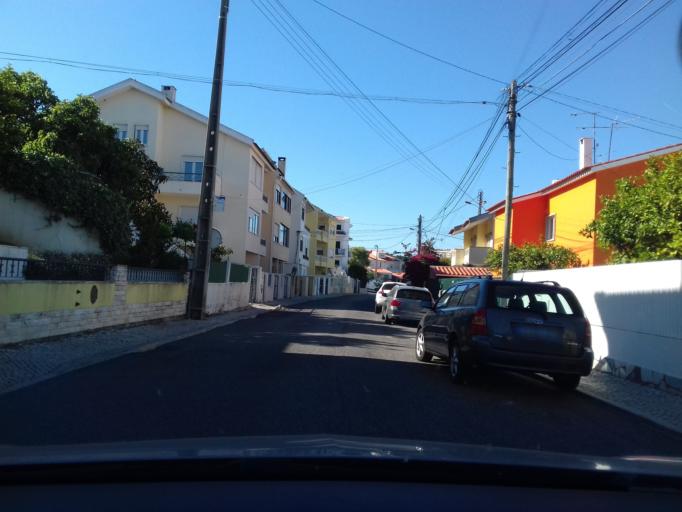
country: PT
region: Lisbon
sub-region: Cascais
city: Alcabideche
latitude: 38.7216
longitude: -9.4099
